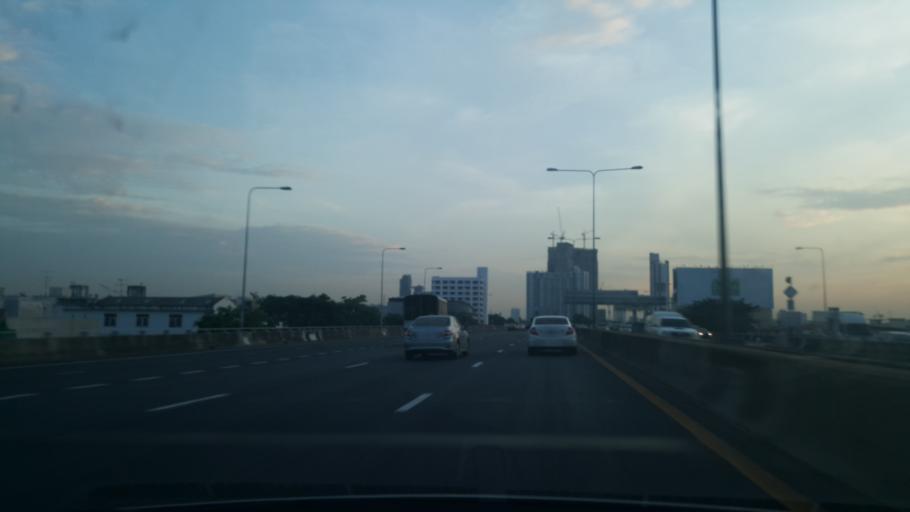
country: TH
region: Bangkok
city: Sathon
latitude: 13.7101
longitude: 100.5193
